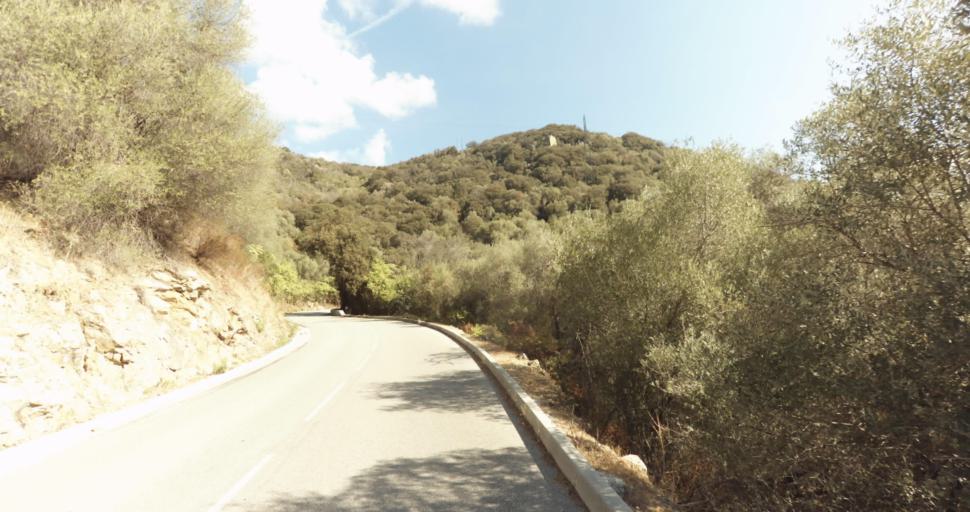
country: FR
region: Corsica
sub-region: Departement de la Corse-du-Sud
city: Ajaccio
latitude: 41.9321
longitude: 8.7036
